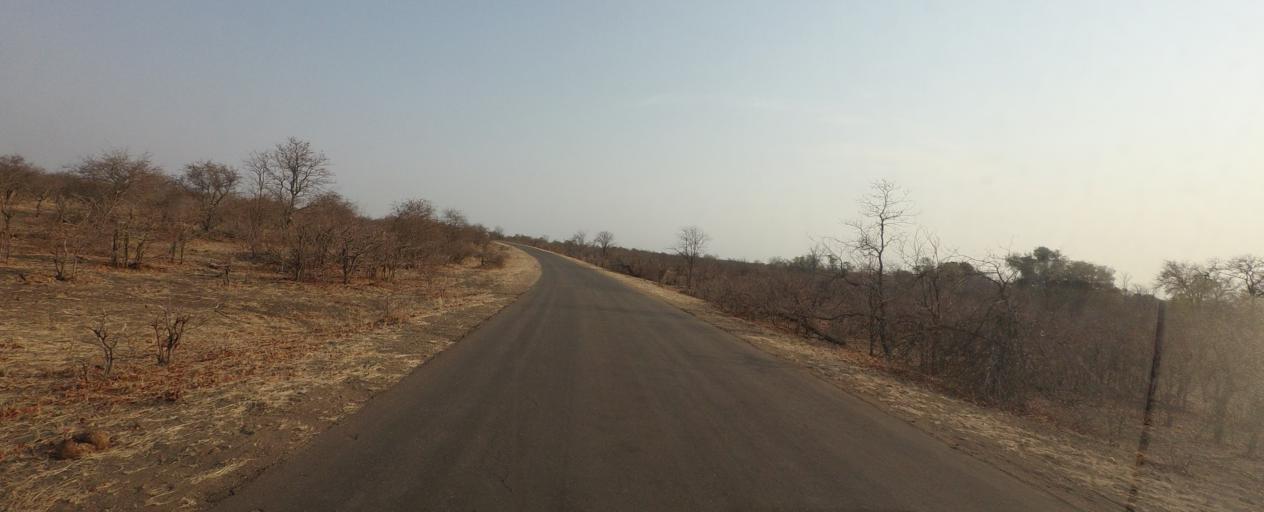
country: ZA
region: Limpopo
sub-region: Mopani District Municipality
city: Giyani
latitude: -23.0889
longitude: 31.4217
